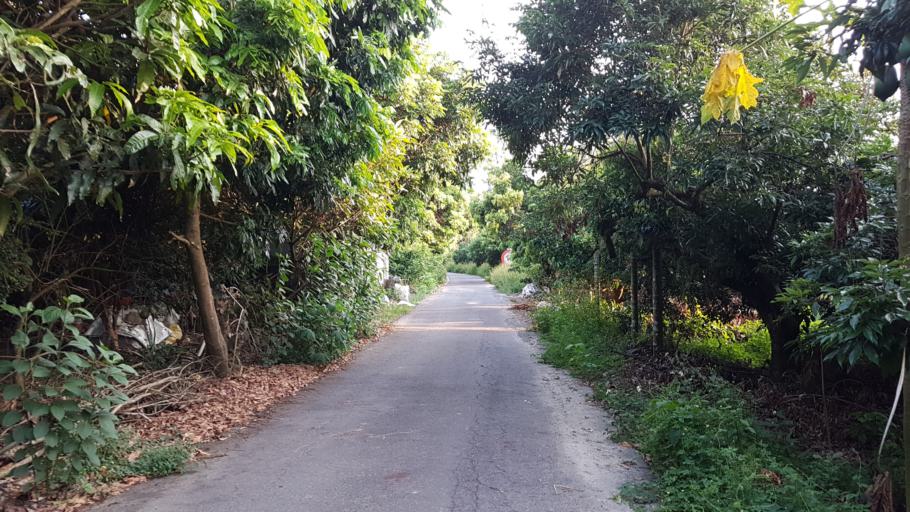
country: TW
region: Taiwan
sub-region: Chiayi
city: Jiayi Shi
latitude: 23.3658
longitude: 120.4643
